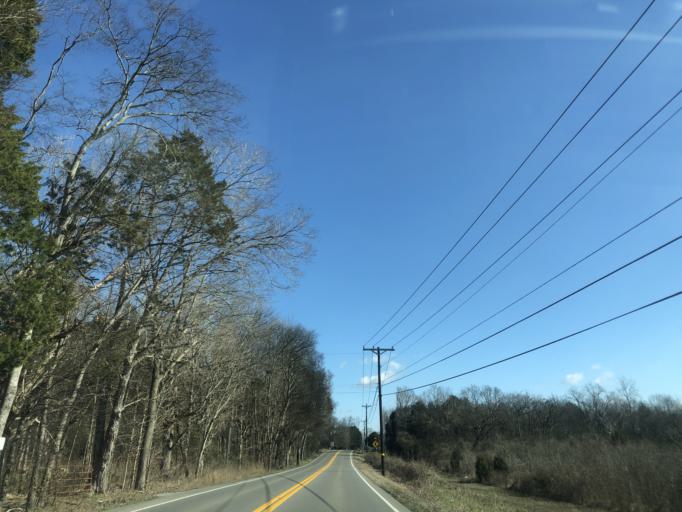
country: US
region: Tennessee
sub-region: Rutherford County
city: Smyrna
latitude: 35.9878
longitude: -86.4239
